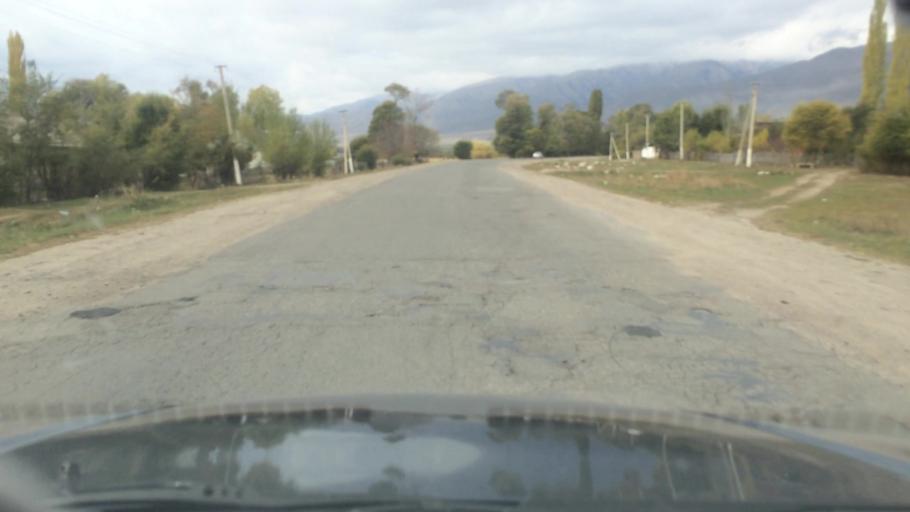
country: KG
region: Ysyk-Koel
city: Tyup
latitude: 42.7823
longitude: 78.2841
